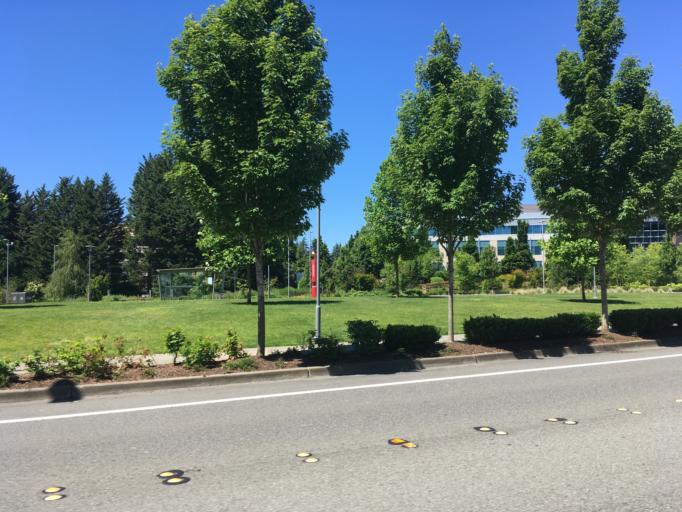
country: US
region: Washington
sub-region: King County
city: Redmond
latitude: 47.6428
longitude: -122.1391
